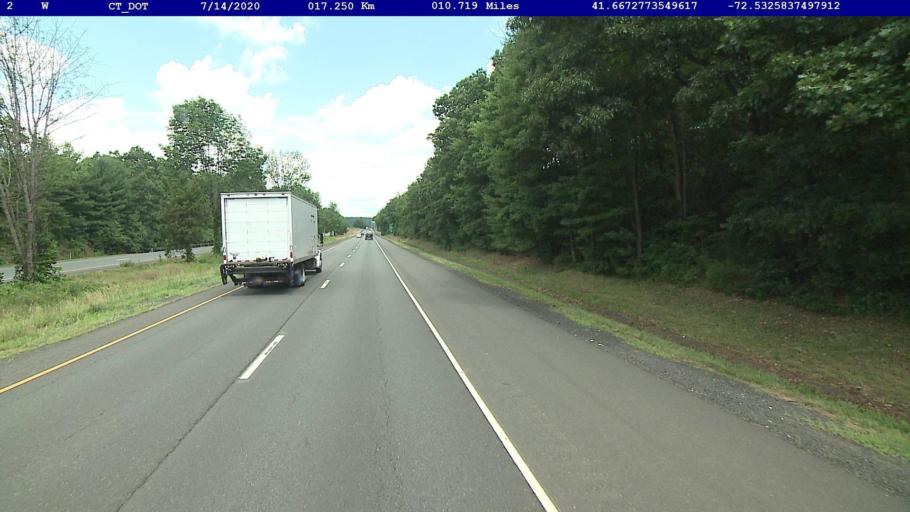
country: US
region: Connecticut
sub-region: Hartford County
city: Terramuggus
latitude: 41.6673
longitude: -72.5326
